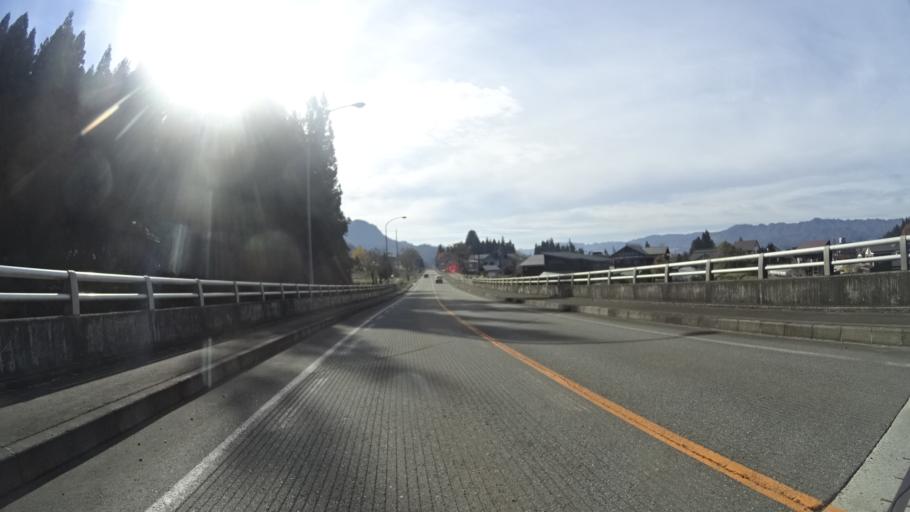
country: JP
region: Niigata
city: Muikamachi
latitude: 37.1327
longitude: 138.9519
